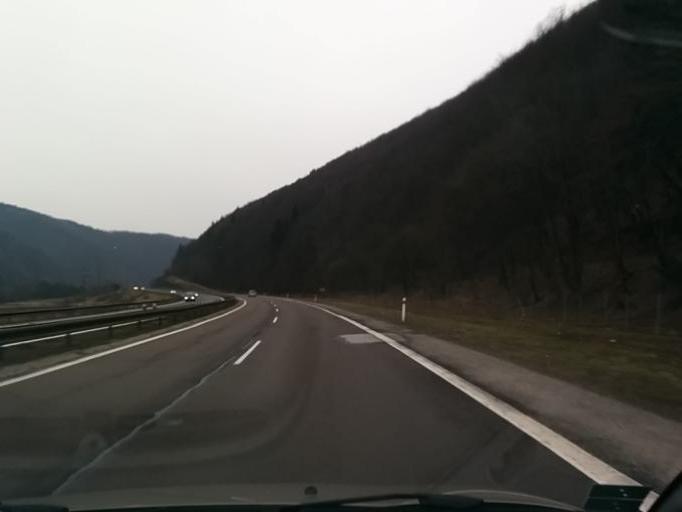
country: SK
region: Banskobystricky
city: Ziar nad Hronom
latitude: 48.5822
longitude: 18.9636
